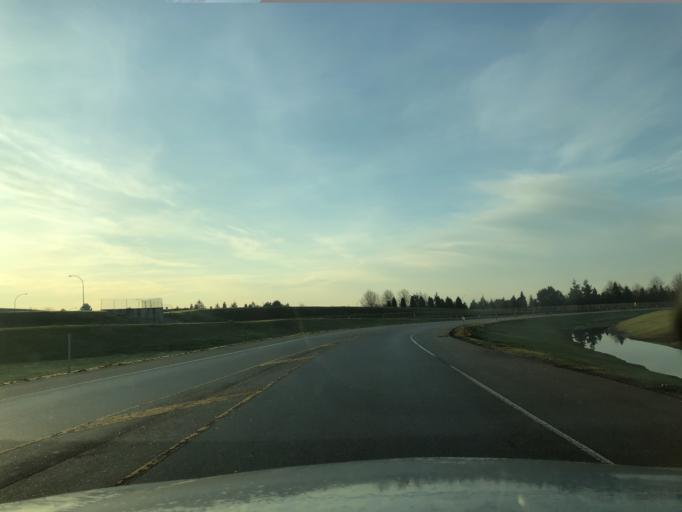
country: CA
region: British Columbia
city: Richmond
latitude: 49.1960
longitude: -123.1519
